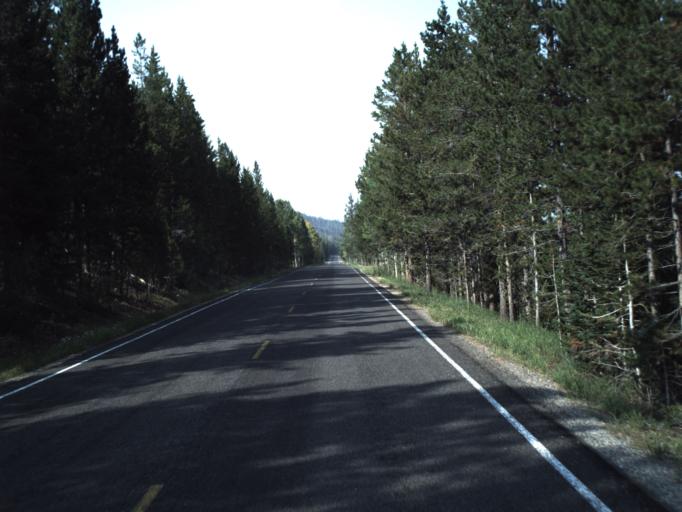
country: US
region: Utah
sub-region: Summit County
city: Kamas
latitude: 40.7909
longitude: -110.8850
